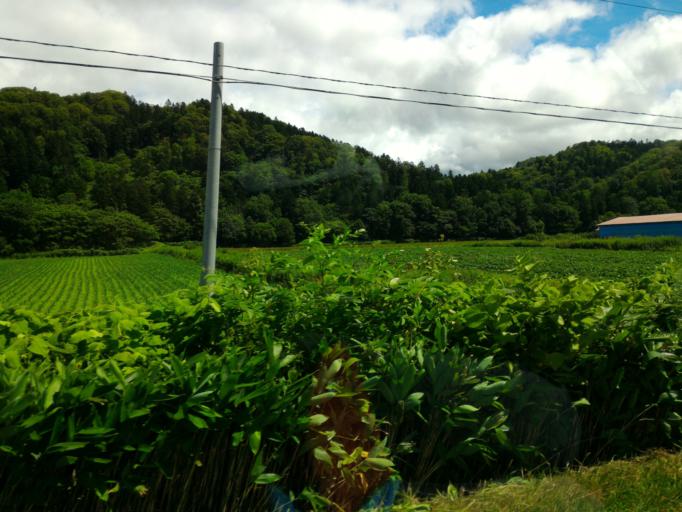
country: JP
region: Hokkaido
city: Nayoro
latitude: 44.6114
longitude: 142.3091
